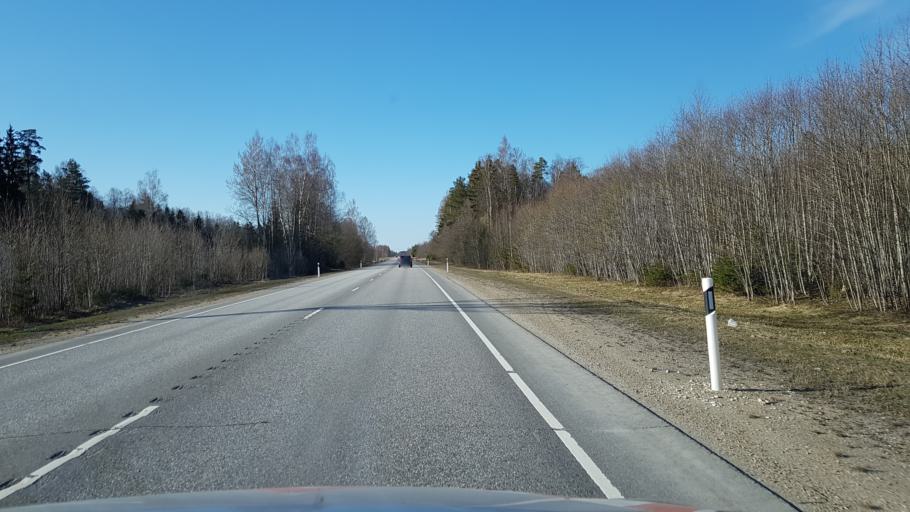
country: EE
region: Ida-Virumaa
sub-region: Johvi vald
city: Johvi
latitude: 59.2048
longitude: 27.3445
